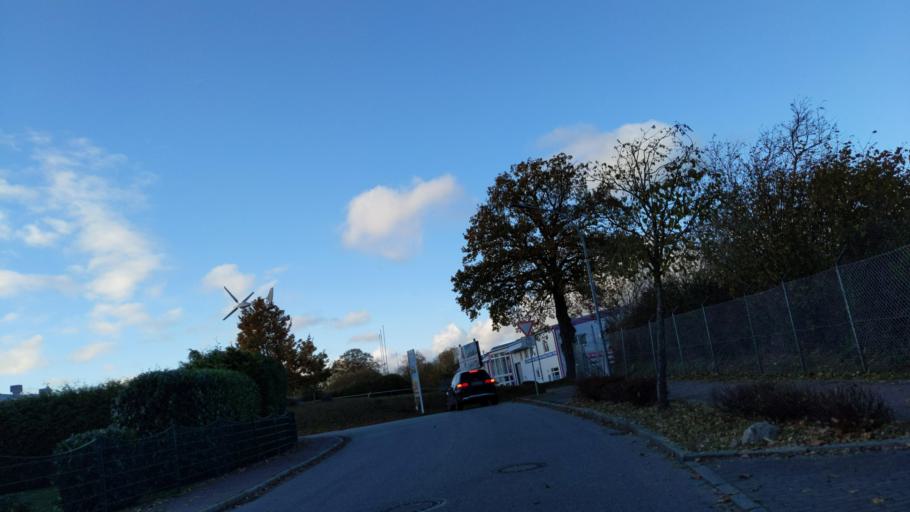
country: DE
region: Schleswig-Holstein
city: Neustadt in Holstein
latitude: 54.0945
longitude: 10.7896
